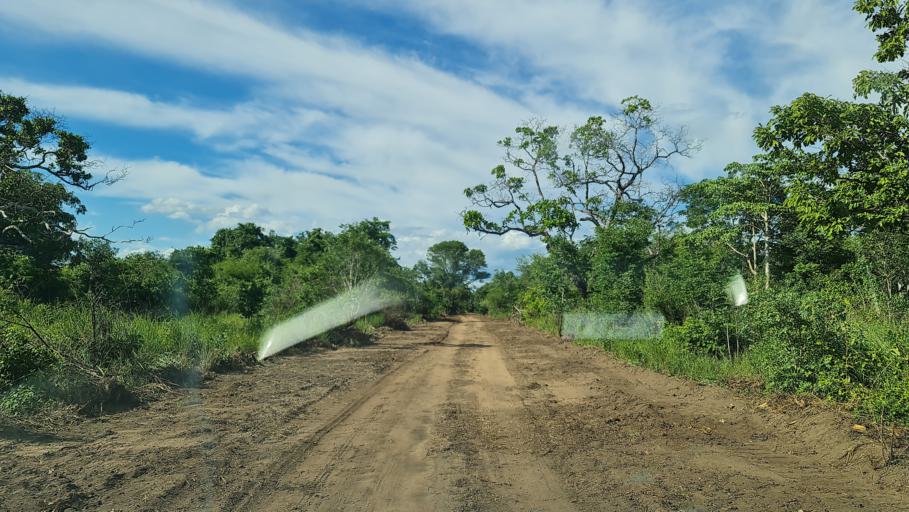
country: MZ
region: Nampula
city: Antonio Enes
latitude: -15.5251
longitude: 40.1270
